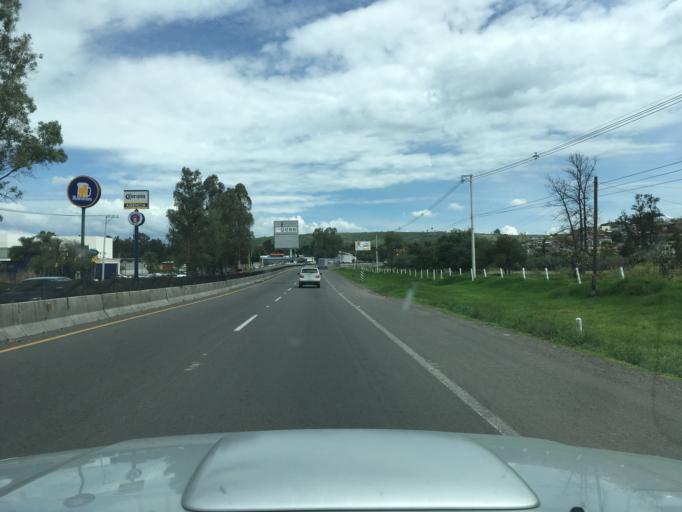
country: MX
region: Michoacan
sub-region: Tarimbaro
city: Conjunto Habitacional el Trebol
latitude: 19.7773
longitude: -101.1571
